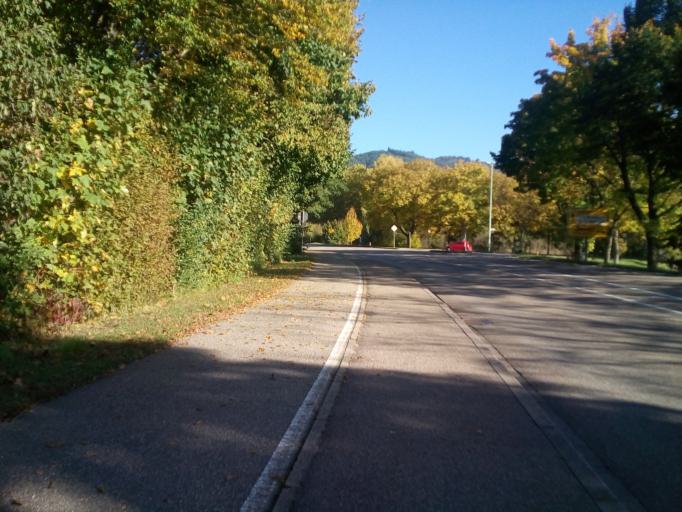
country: DE
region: Baden-Wuerttemberg
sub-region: Karlsruhe Region
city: Buhl
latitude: 48.6863
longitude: 8.1378
